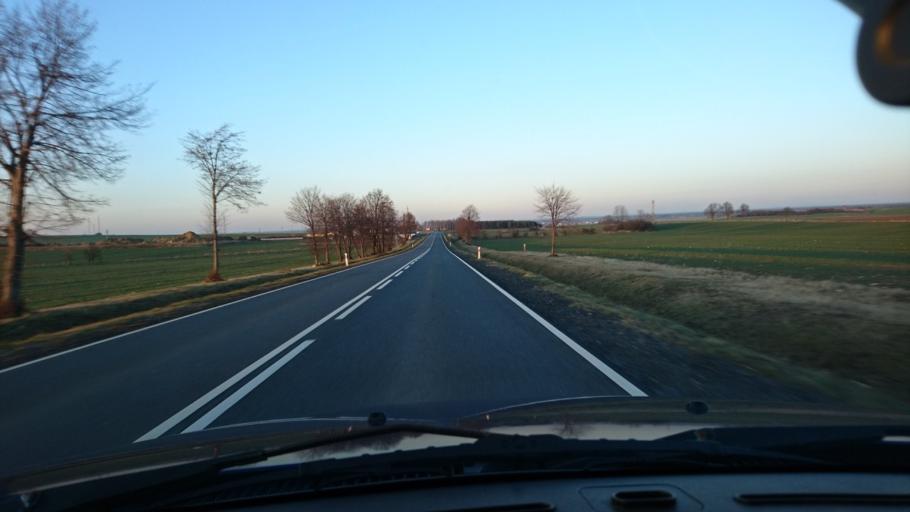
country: PL
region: Silesian Voivodeship
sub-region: Powiat gliwicki
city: Wielowies
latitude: 50.4875
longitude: 18.6054
